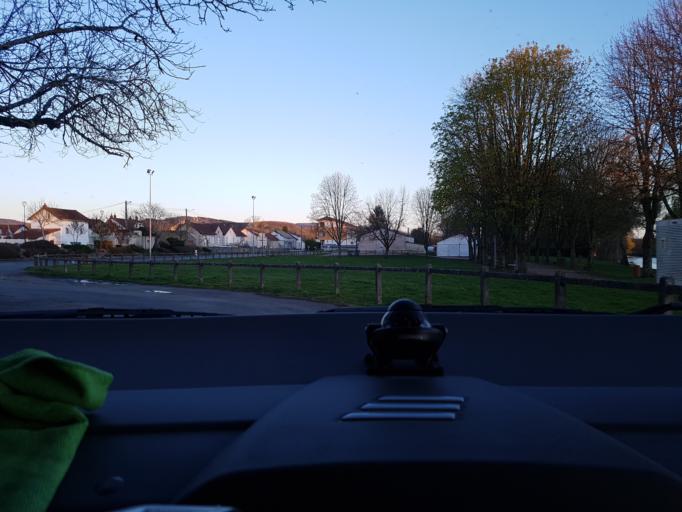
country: FR
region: Bourgogne
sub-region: Departement de Saone-et-Loire
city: Etang-sur-Arroux
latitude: 46.8652
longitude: 4.1890
